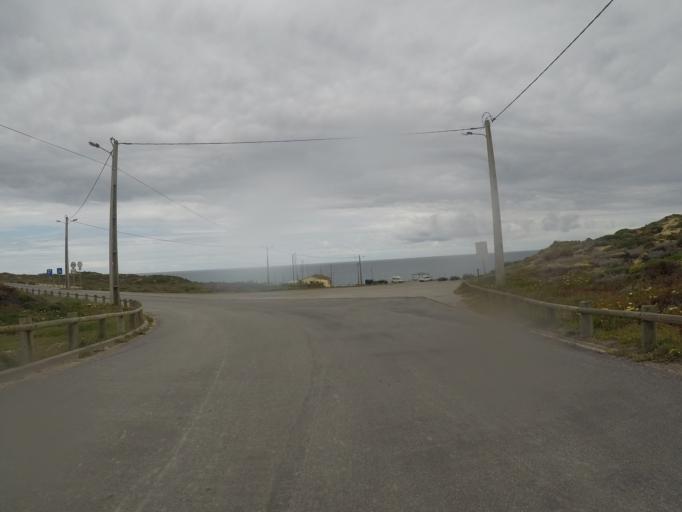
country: PT
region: Beja
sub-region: Odemira
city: Vila Nova de Milfontes
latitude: 37.6530
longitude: -8.8000
